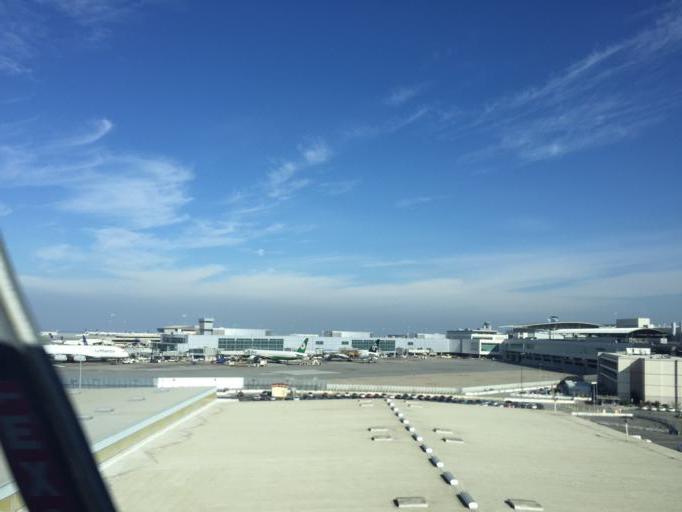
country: US
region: California
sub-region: San Mateo County
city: San Bruno
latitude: 37.6165
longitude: -122.3975
